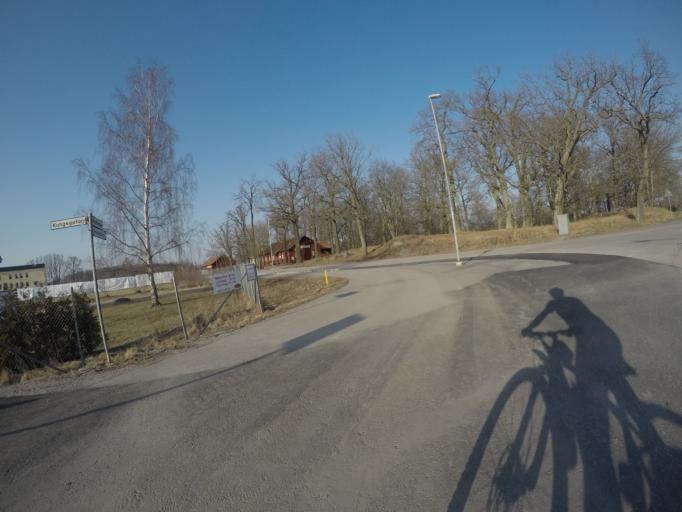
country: SE
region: Vaestmanland
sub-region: Kungsors Kommun
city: Kungsoer
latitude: 59.4263
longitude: 16.1117
